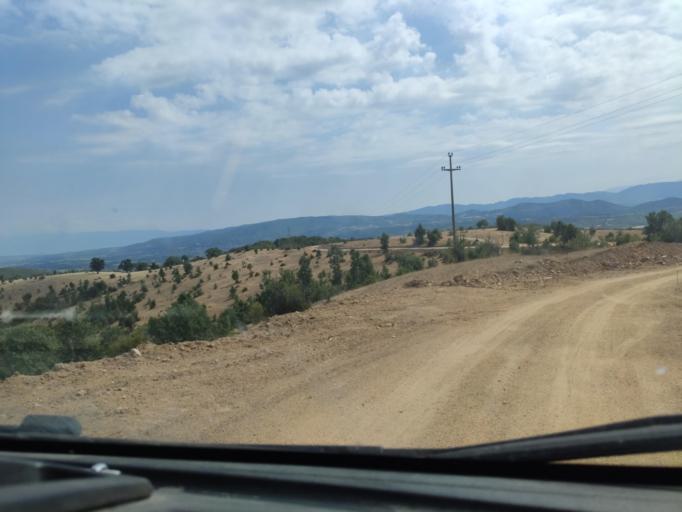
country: MK
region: Radovis
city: Radovish
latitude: 41.6700
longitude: 22.4053
